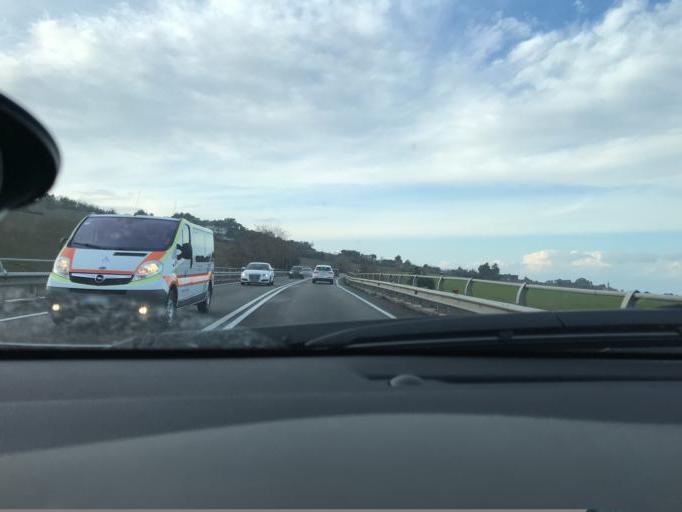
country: IT
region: The Marches
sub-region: Provincia di Ancona
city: Falconara Marittima
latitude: 43.6049
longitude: 13.4202
